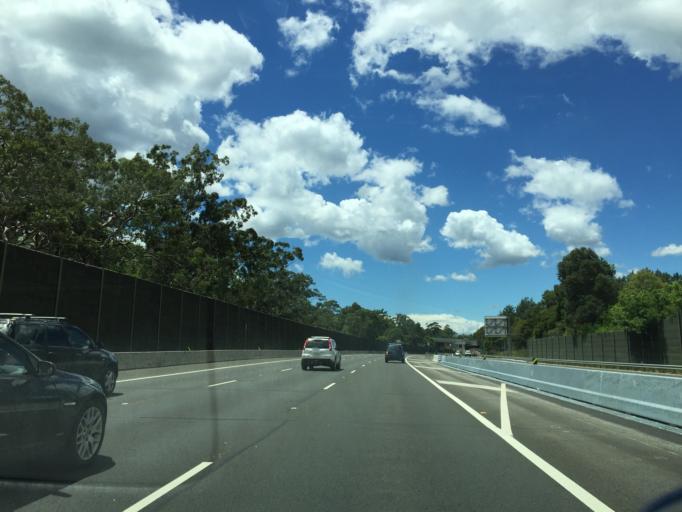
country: AU
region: New South Wales
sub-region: Parramatta
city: Epping
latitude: -33.7621
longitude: 151.0744
